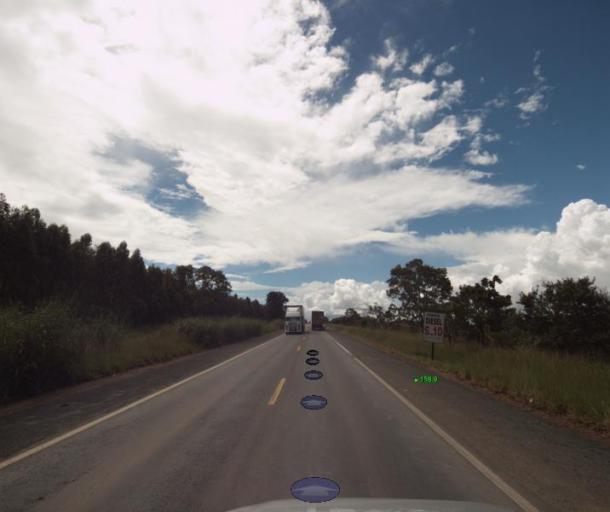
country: BR
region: Goias
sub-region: Uruacu
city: Uruacu
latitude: -14.1717
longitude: -49.1247
